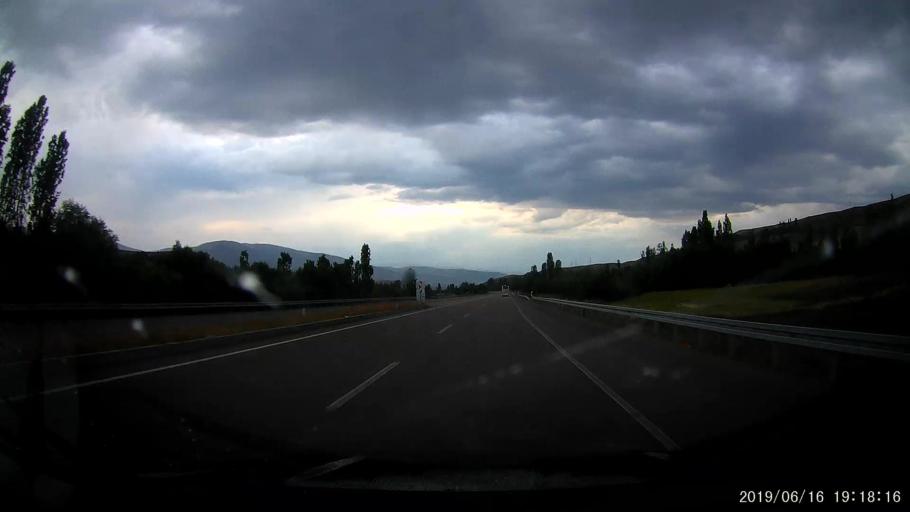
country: TR
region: Sivas
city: Akincilar
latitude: 40.0950
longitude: 38.4627
